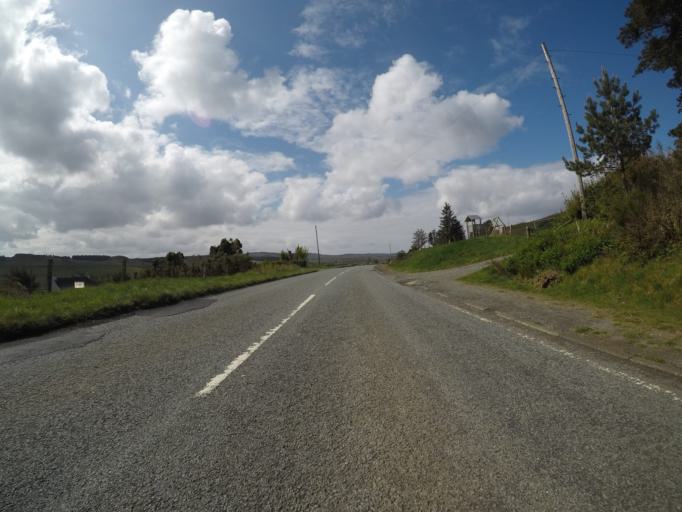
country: GB
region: Scotland
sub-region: Highland
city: Isle of Skye
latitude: 57.4515
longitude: -6.2888
